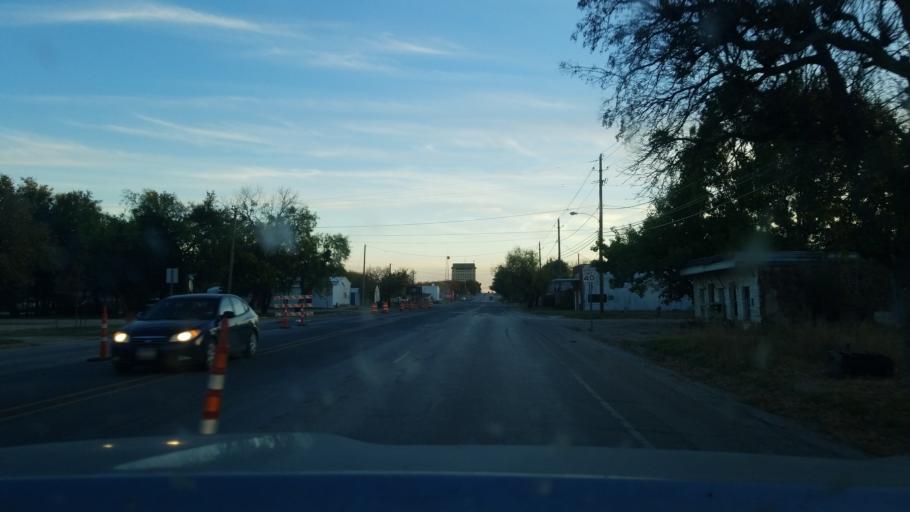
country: US
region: Texas
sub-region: Stephens County
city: Breckenridge
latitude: 32.7636
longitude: -98.9028
